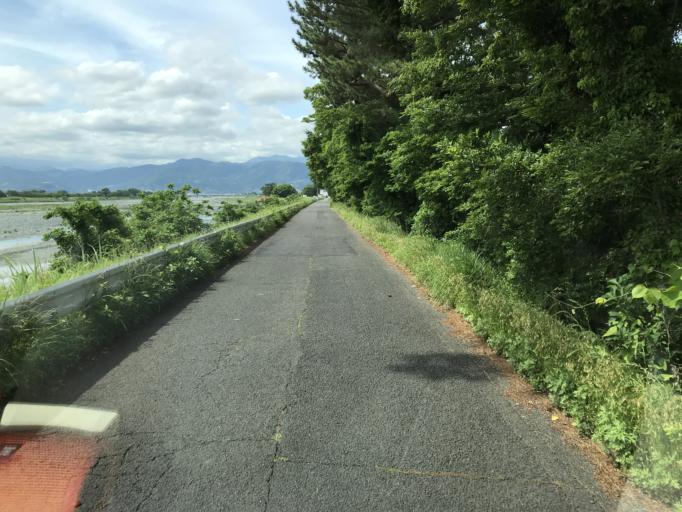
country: JP
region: Kanagawa
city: Odawara
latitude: 35.2977
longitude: 139.1575
